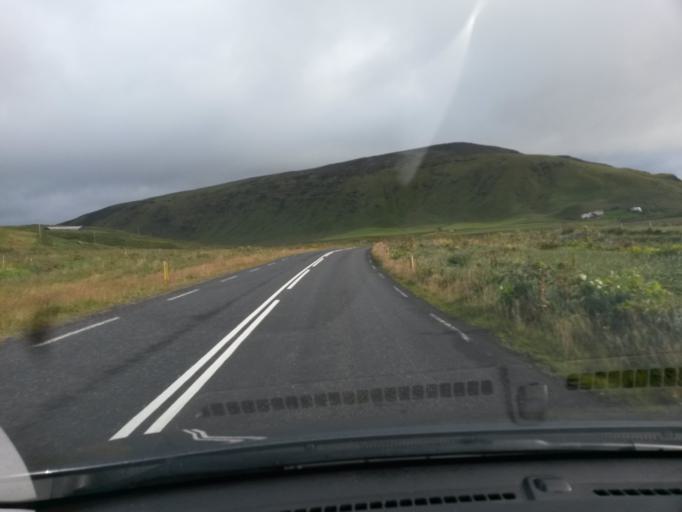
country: IS
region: South
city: Vestmannaeyjar
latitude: 63.4454
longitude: -19.1392
